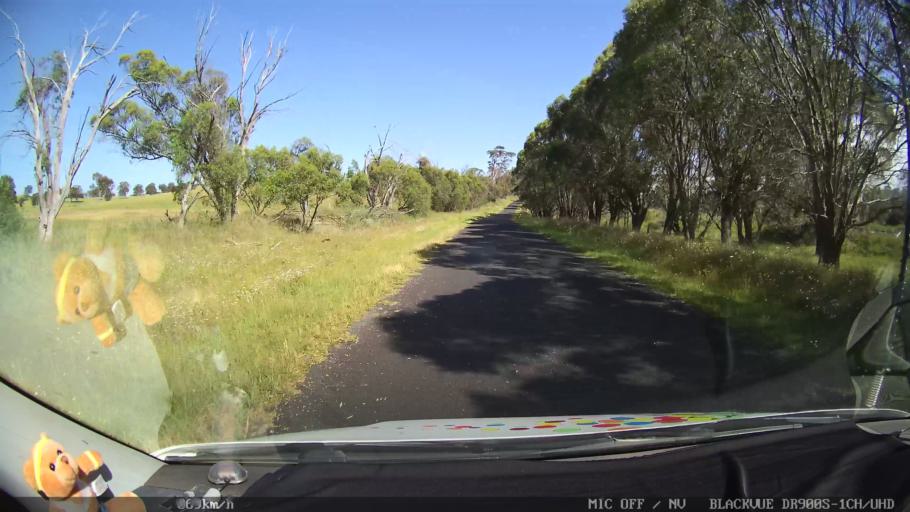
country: AU
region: New South Wales
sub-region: Guyra
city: Guyra
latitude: -30.0664
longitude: 151.6673
